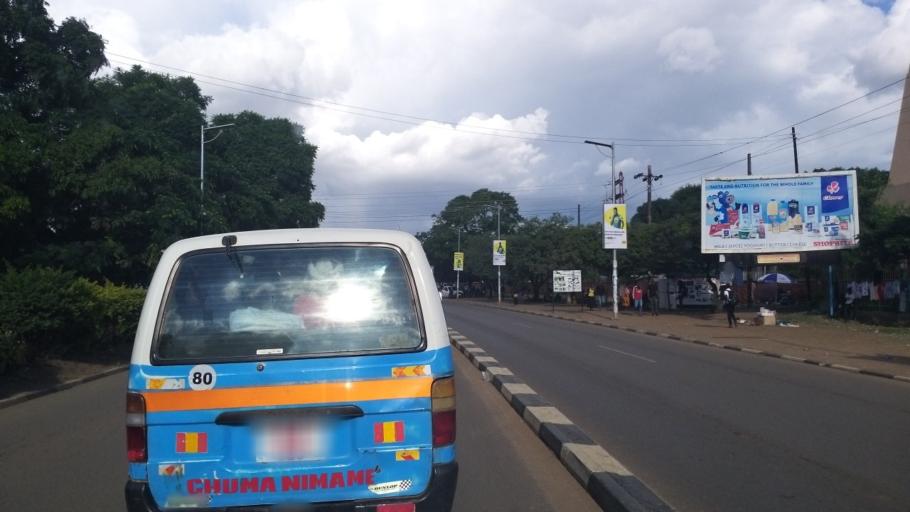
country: ZM
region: Lusaka
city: Lusaka
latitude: -15.4241
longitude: 28.2886
